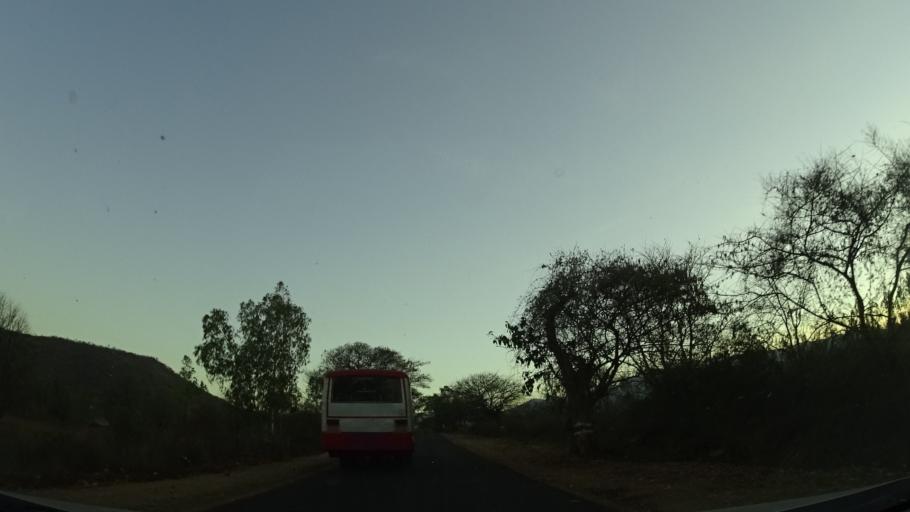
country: IN
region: Karnataka
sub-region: Chikmagalur
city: Tarikere
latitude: 13.5820
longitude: 75.8370
